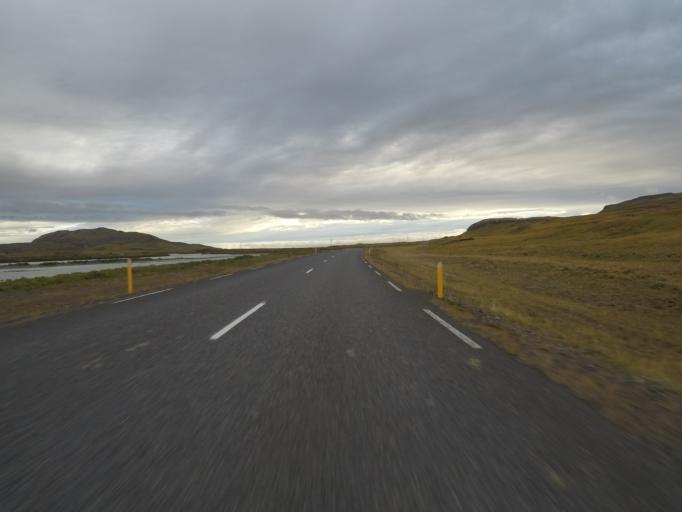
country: IS
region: South
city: Vestmannaeyjar
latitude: 64.0597
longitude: -20.1197
